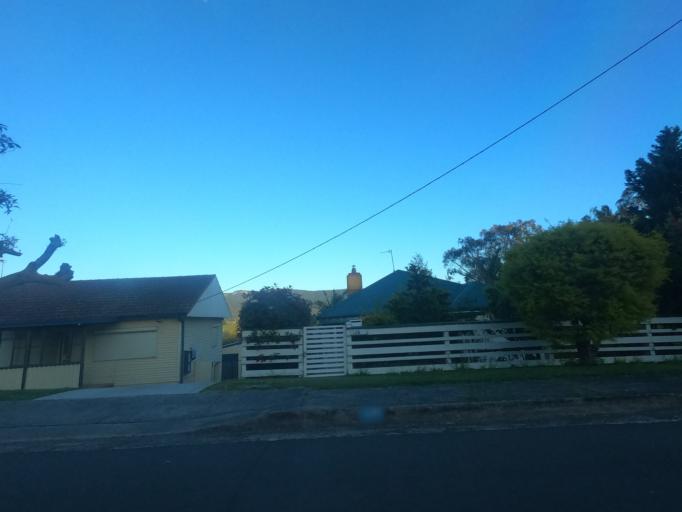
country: AU
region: New South Wales
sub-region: Wollongong
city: Dapto
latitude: -34.5051
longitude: 150.7857
